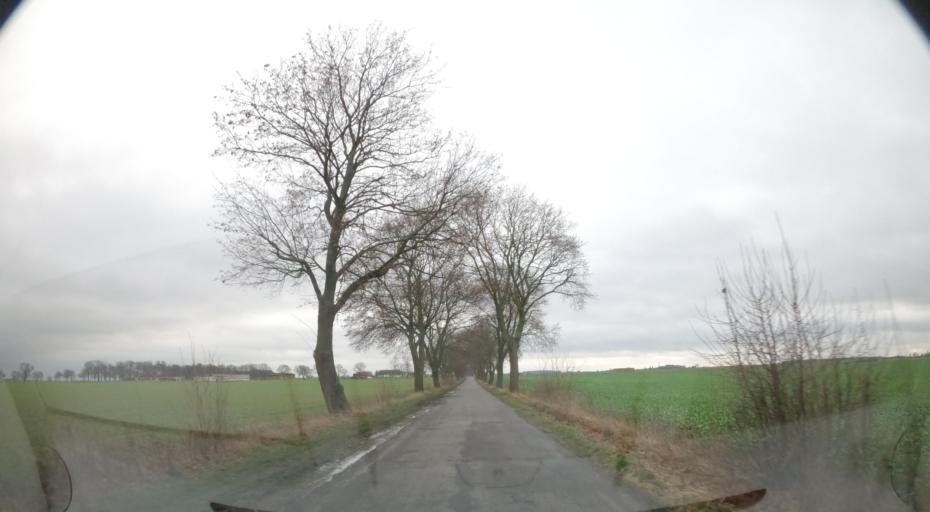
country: PL
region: Greater Poland Voivodeship
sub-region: Powiat pilski
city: Wysoka
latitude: 53.2735
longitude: 17.1005
